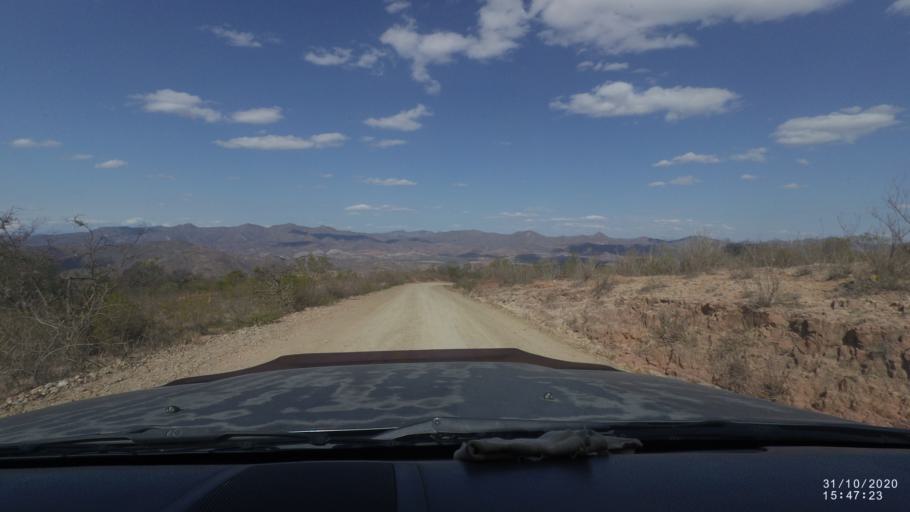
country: BO
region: Chuquisaca
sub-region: Provincia Zudanez
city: Mojocoya
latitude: -18.3136
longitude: -64.7149
